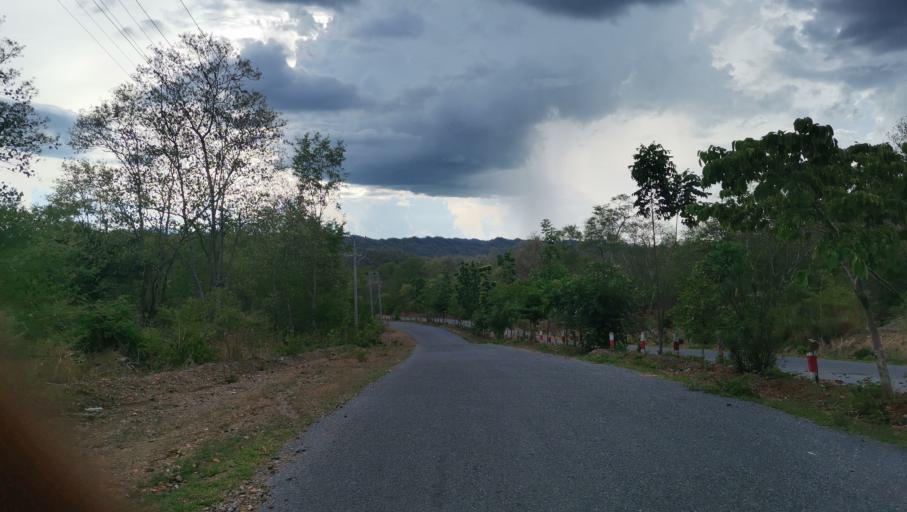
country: MM
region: Magway
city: Minbu
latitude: 20.1061
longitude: 94.5431
